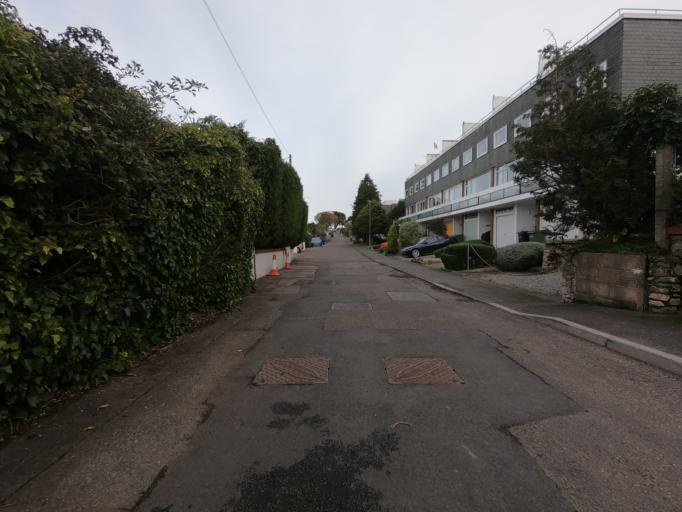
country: GB
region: England
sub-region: Borough of Torbay
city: Brixham
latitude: 50.3982
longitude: -3.5052
